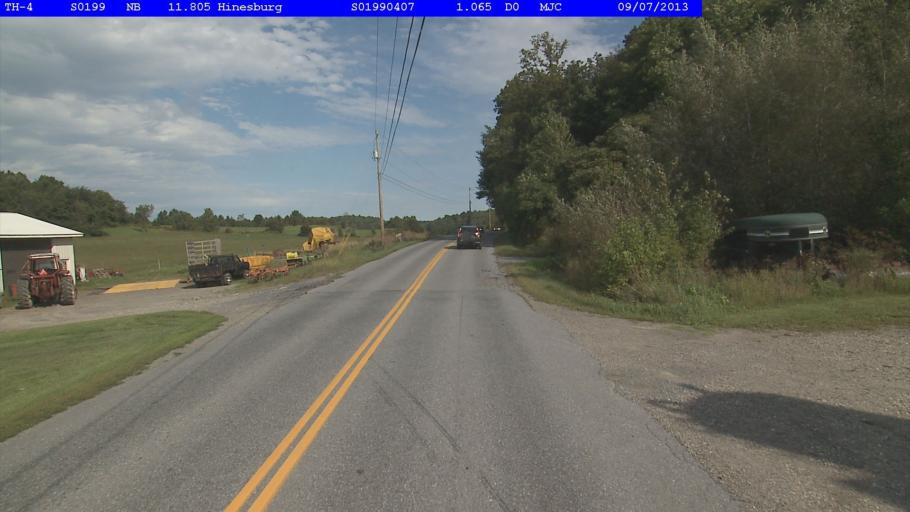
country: US
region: Vermont
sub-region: Chittenden County
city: Hinesburg
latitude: 44.2933
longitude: -73.1083
